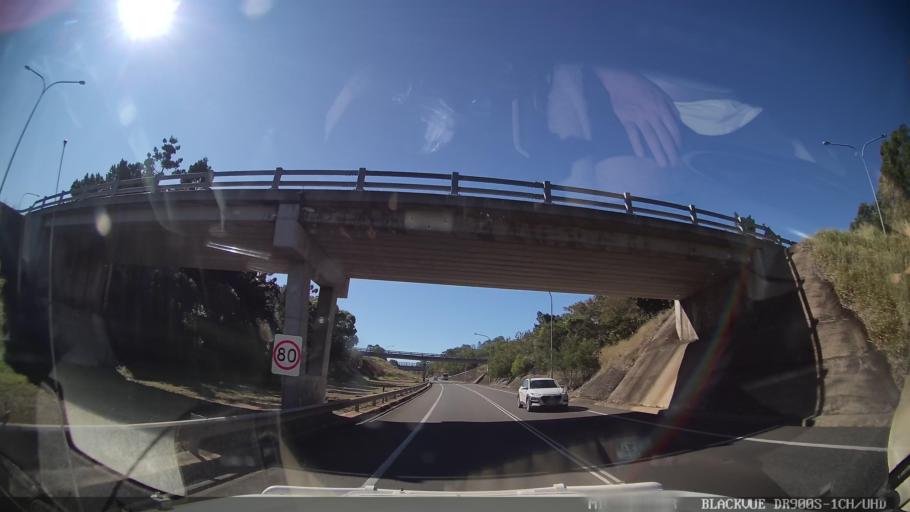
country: AU
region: Queensland
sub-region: Fraser Coast
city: Maryborough
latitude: -25.5202
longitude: 152.6682
